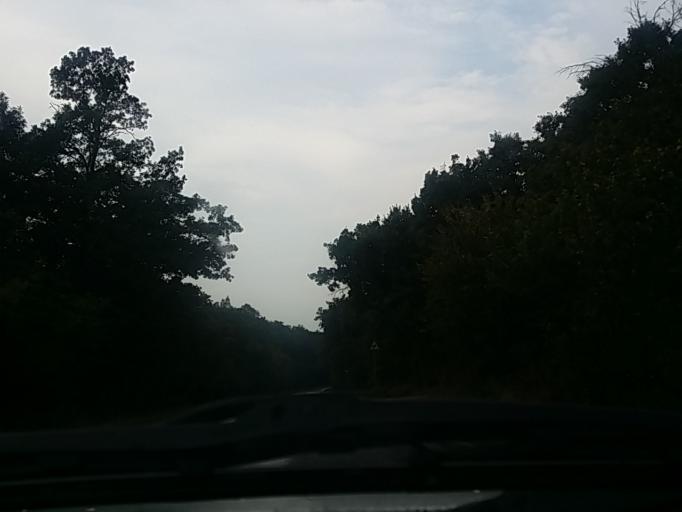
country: HU
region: Pest
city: Paty
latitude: 47.5018
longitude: 18.8638
